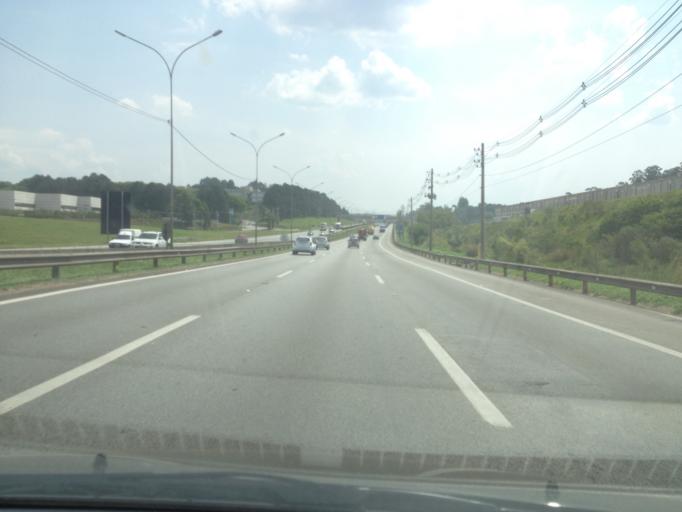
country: BR
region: Sao Paulo
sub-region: Jandira
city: Jandira
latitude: -23.5170
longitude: -46.9302
